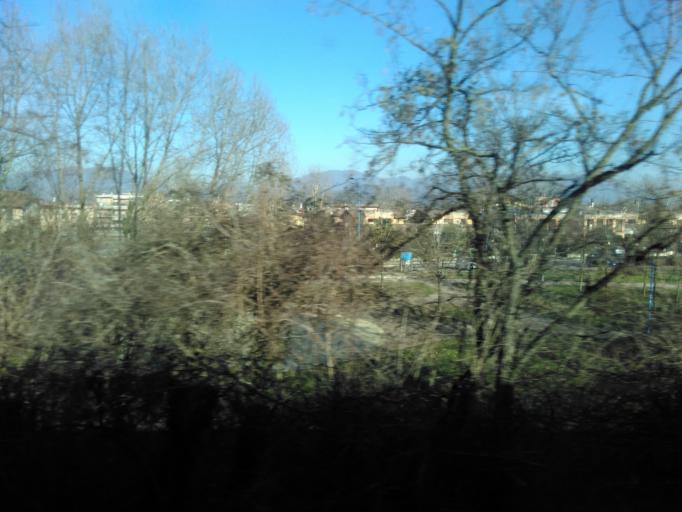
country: IT
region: Lombardy
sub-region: Provincia di Brescia
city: Roncadelle
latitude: 45.5396
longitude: 10.1656
